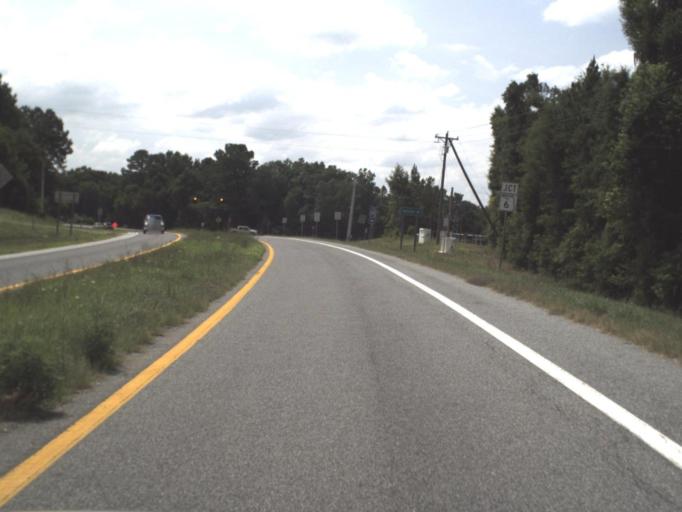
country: US
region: Florida
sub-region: Hamilton County
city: Jasper
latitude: 30.5309
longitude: -83.0434
